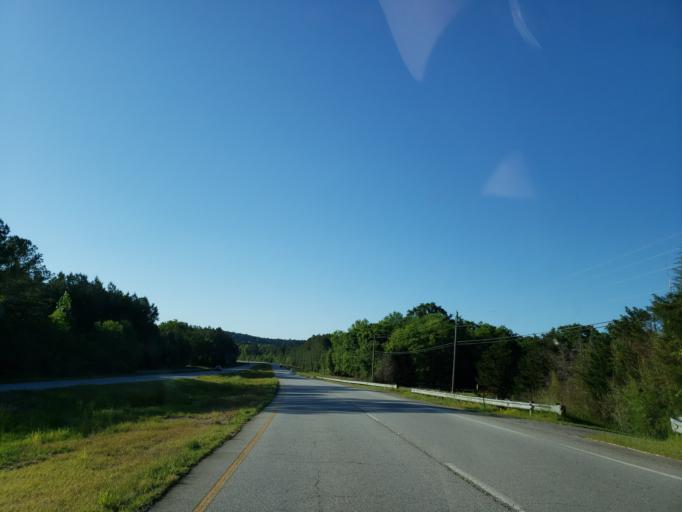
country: US
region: Georgia
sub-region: Polk County
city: Cedartown
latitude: 33.9458
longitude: -85.2434
